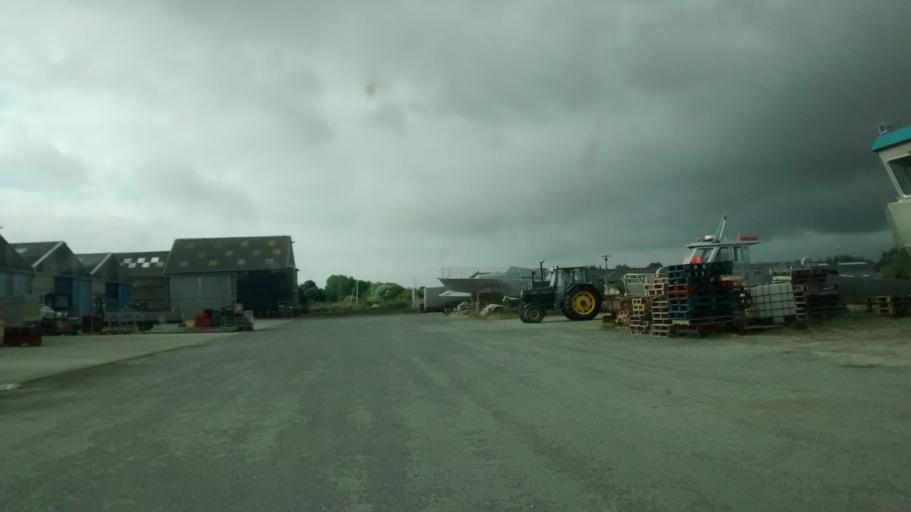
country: FR
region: Brittany
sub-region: Departement d'Ille-et-Vilaine
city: Le Vivier-sur-Mer
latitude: 48.6052
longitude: -1.7693
